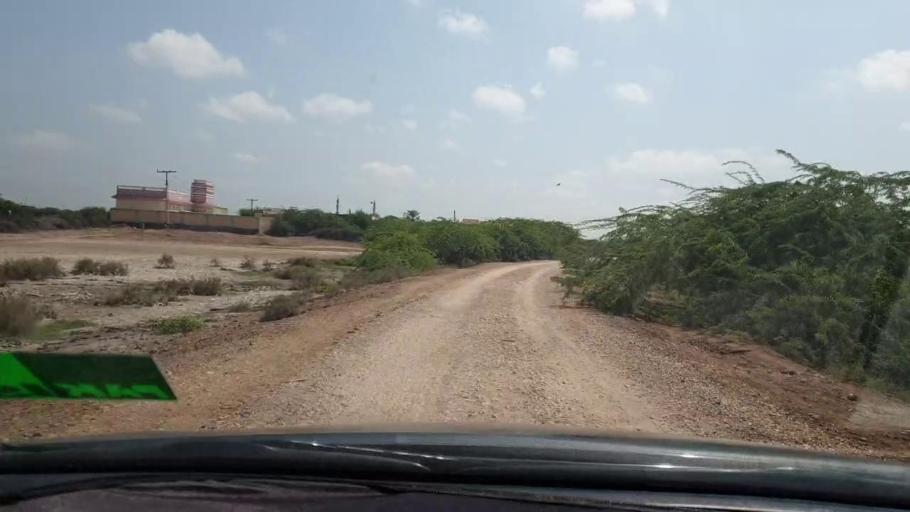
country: PK
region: Sindh
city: Digri
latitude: 24.9507
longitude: 69.1120
